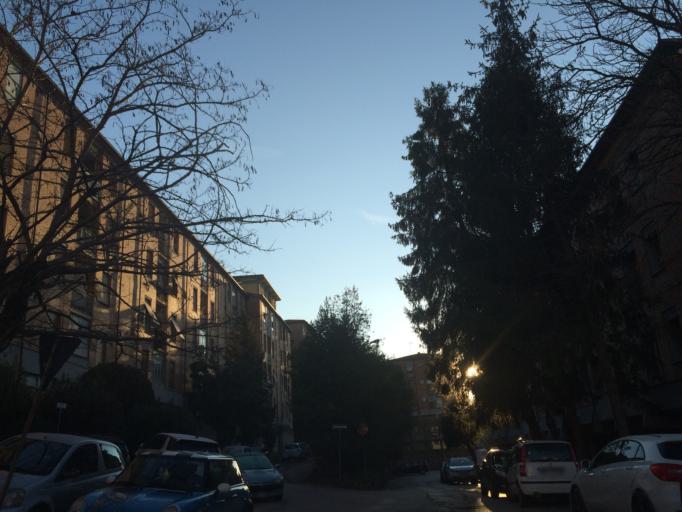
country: IT
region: Umbria
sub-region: Provincia di Perugia
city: Perugia
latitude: 43.1017
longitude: 12.3811
